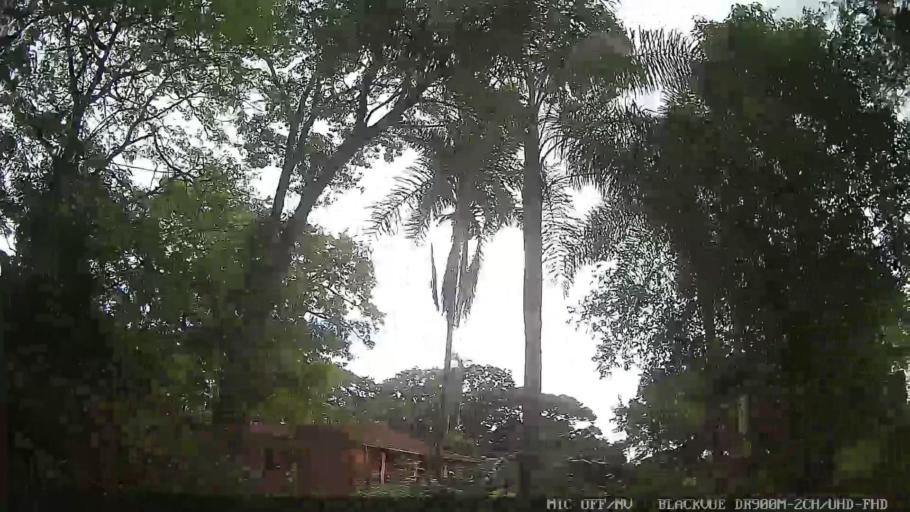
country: BR
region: Sao Paulo
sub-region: Jaguariuna
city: Jaguariuna
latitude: -22.6663
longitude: -46.9772
